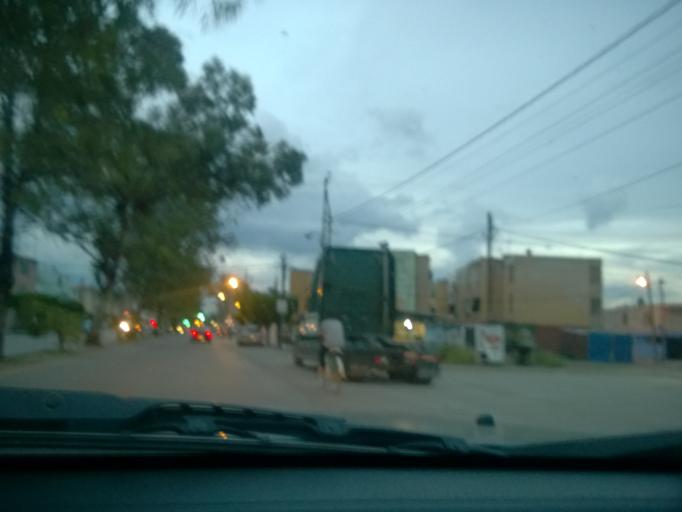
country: MX
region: Guanajuato
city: Leon
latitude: 21.1320
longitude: -101.6471
